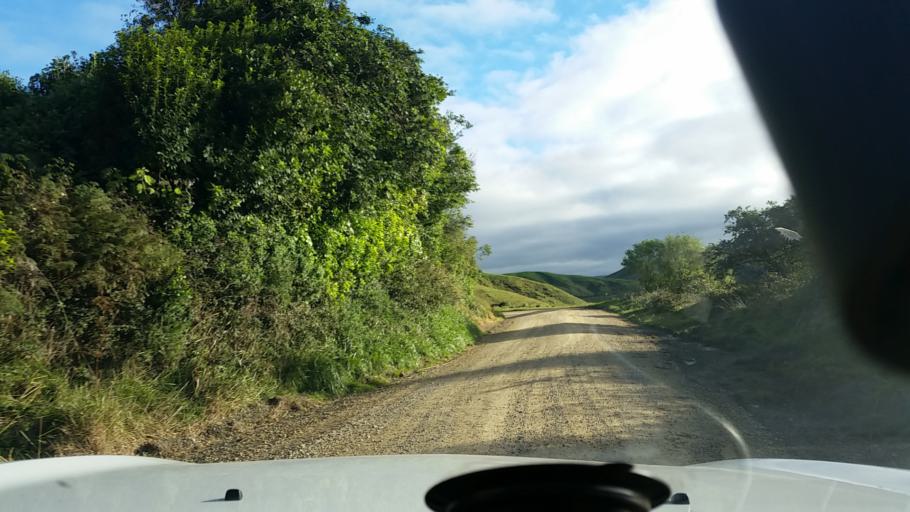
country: NZ
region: Hawke's Bay
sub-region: Napier City
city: Napier
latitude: -39.2604
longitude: 176.8485
